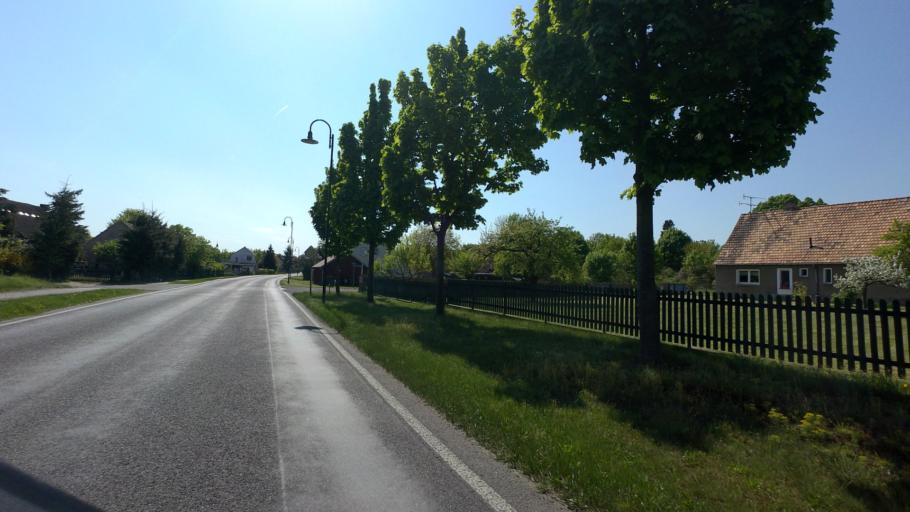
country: DE
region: Brandenburg
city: Tauche
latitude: 52.0656
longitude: 14.1472
